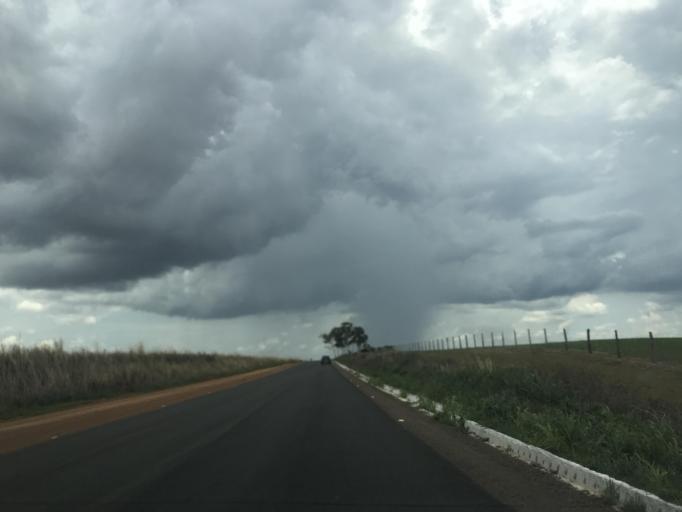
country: BR
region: Goias
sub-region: Vianopolis
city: Vianopolis
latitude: -16.8286
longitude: -48.5297
